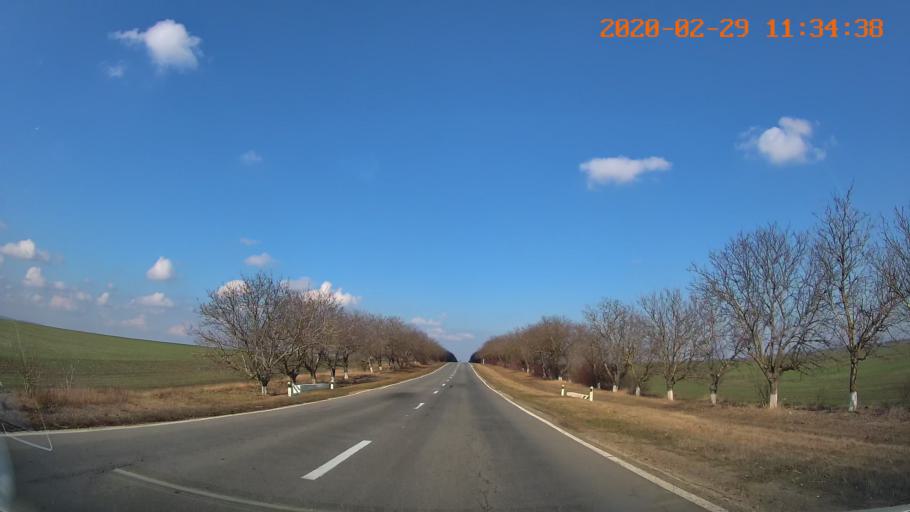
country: MD
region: Rezina
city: Saharna
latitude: 47.5686
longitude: 29.0716
